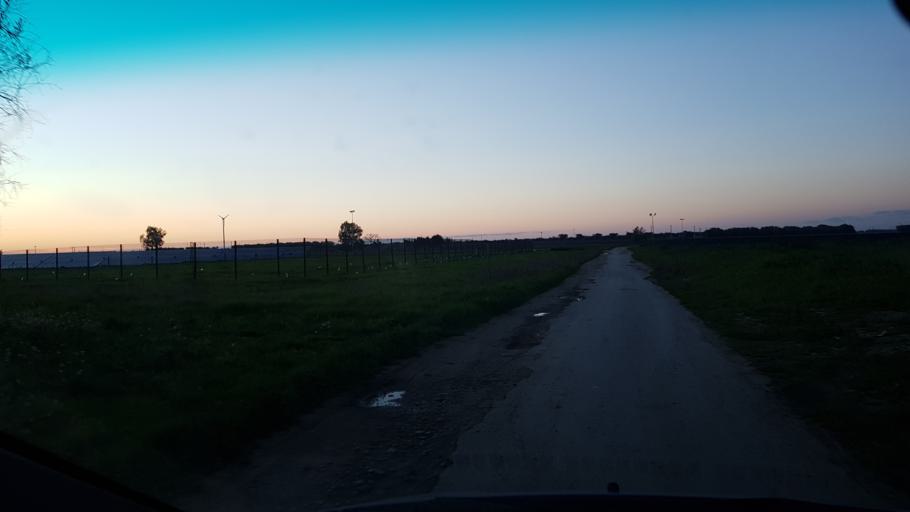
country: IT
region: Apulia
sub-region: Provincia di Brindisi
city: San Pietro Vernotico
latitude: 40.5081
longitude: 17.9720
